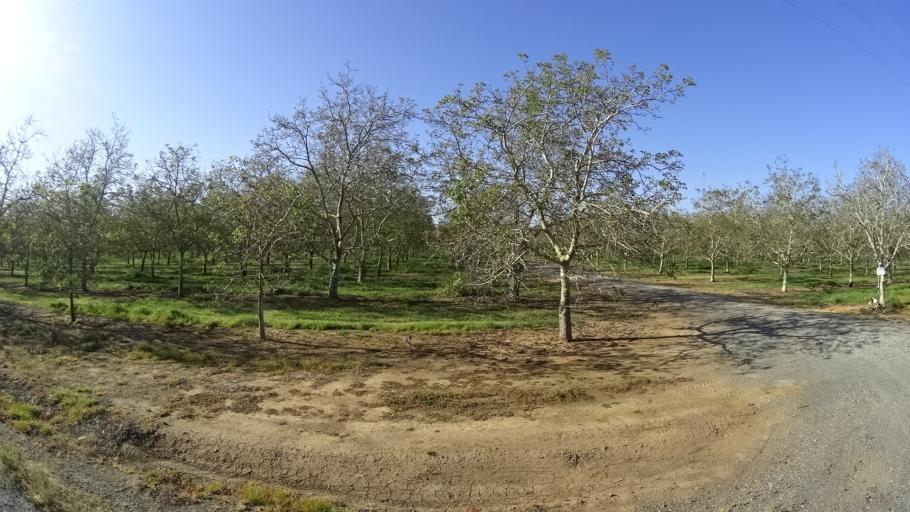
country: US
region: California
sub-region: Glenn County
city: Orland
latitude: 39.6820
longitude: -122.1647
